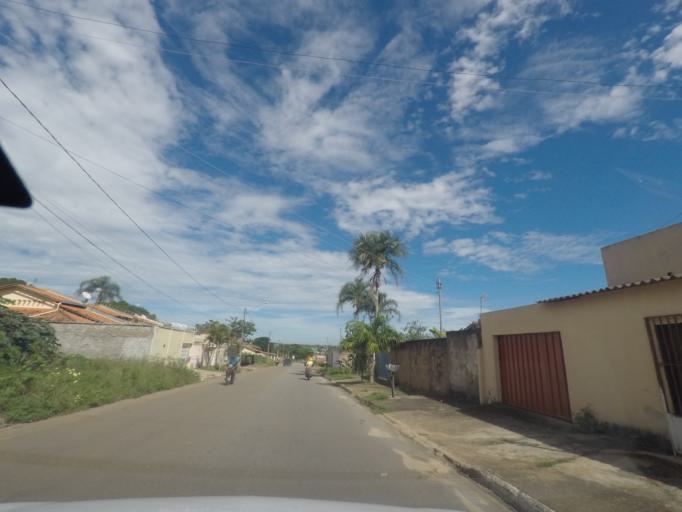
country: BR
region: Goias
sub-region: Aparecida De Goiania
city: Aparecida de Goiania
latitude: -16.8122
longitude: -49.2907
